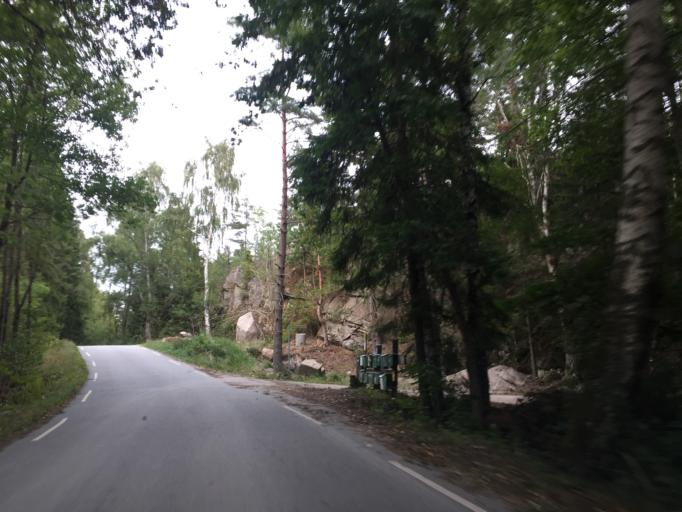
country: NO
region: Ostfold
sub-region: Hvaler
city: Skjaerhalden
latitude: 59.0609
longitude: 11.0649
